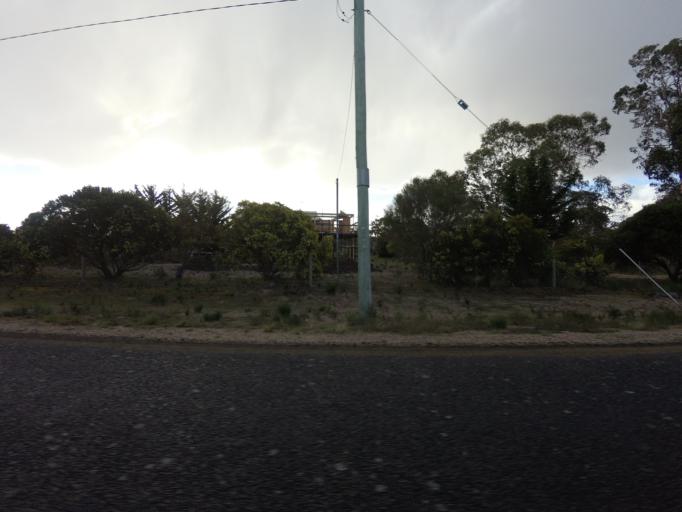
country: AU
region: Tasmania
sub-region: Break O'Day
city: St Helens
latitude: -42.1006
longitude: 148.0840
